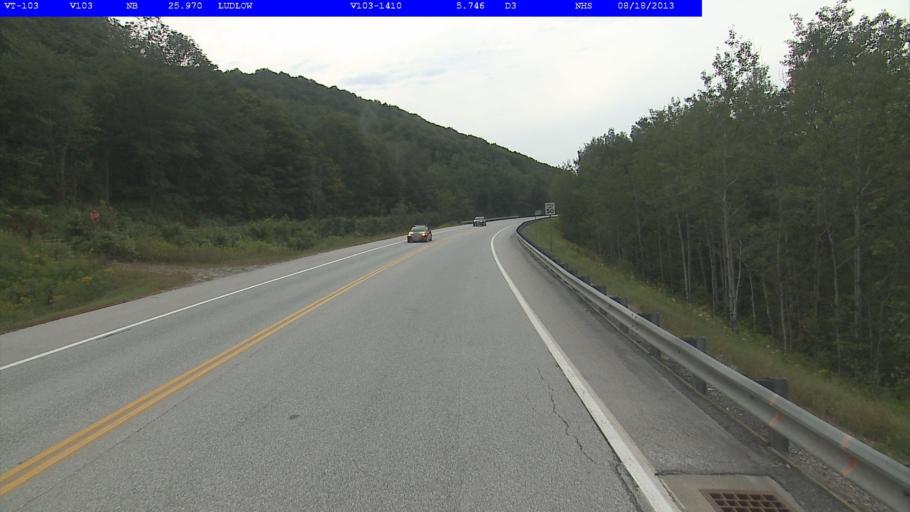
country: US
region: Vermont
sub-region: Windsor County
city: Chester
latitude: 43.4347
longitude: -72.7323
